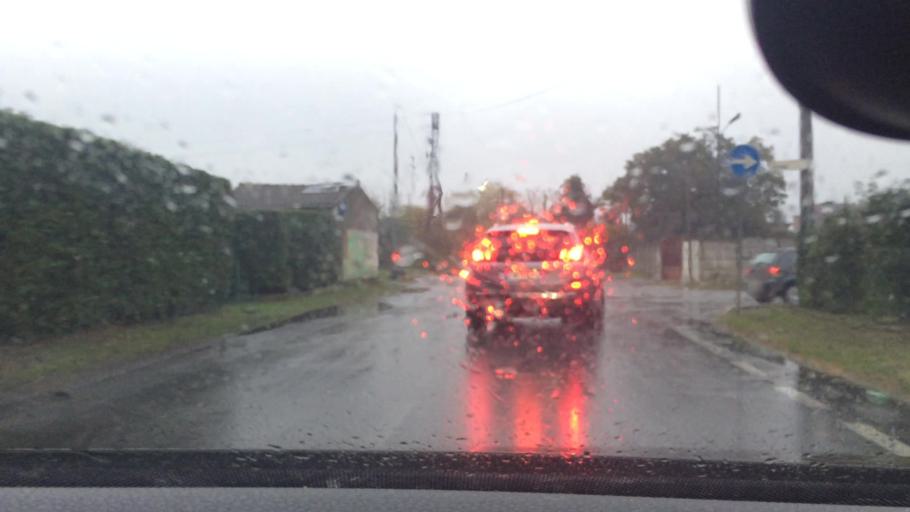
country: IT
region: Lombardy
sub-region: Citta metropolitana di Milano
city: Vanzago
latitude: 45.5317
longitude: 8.9818
